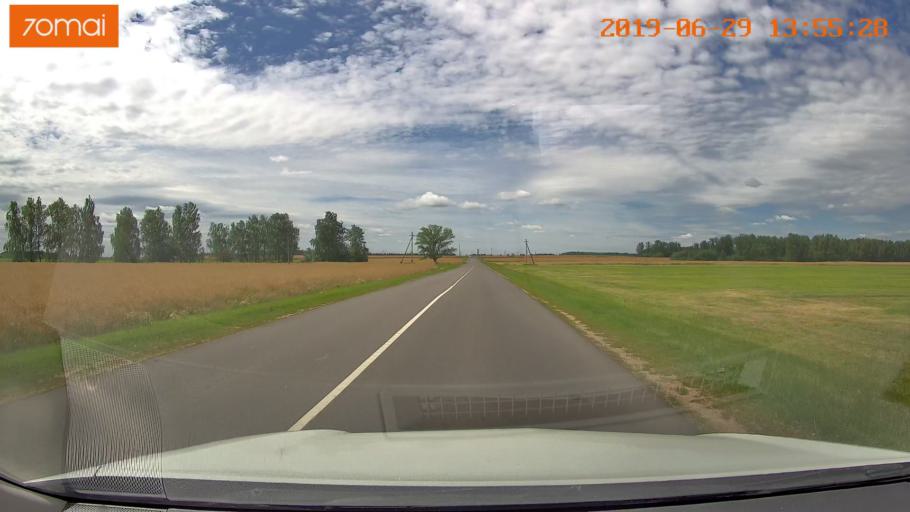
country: BY
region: Minsk
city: Slutsk
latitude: 52.9840
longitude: 27.5195
